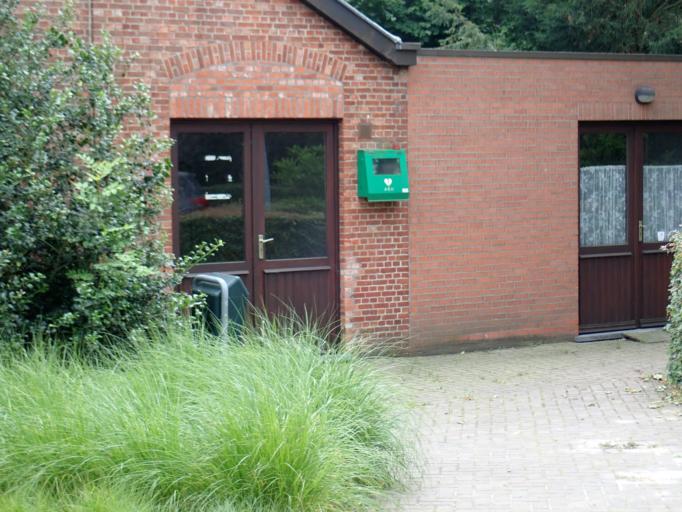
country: BE
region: Flanders
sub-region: Provincie Antwerpen
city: Baarle-Hertog
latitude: 51.4066
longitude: 4.8931
